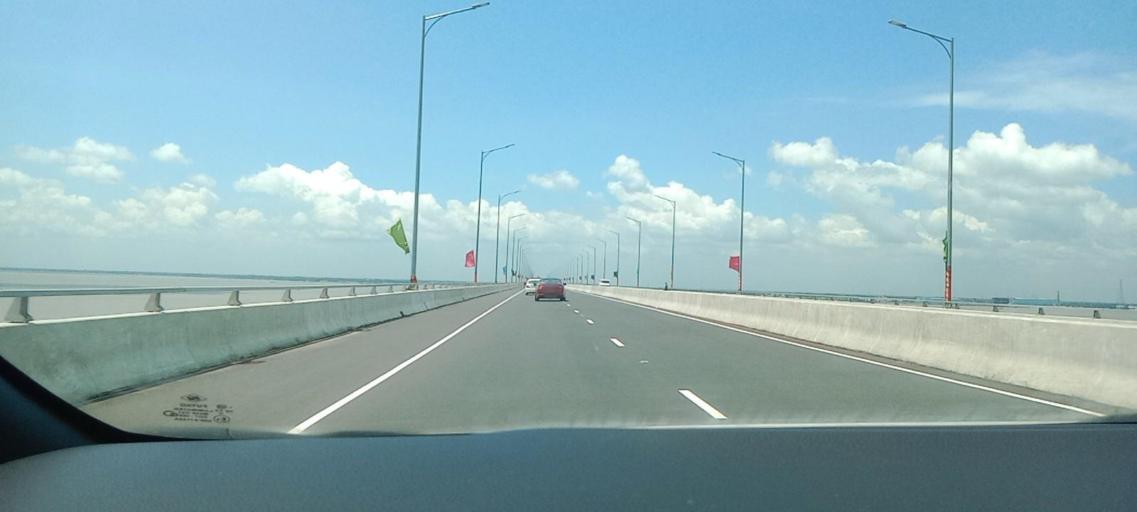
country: BD
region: Dhaka
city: Char Bhadrasan
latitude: 23.4337
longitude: 90.2605
